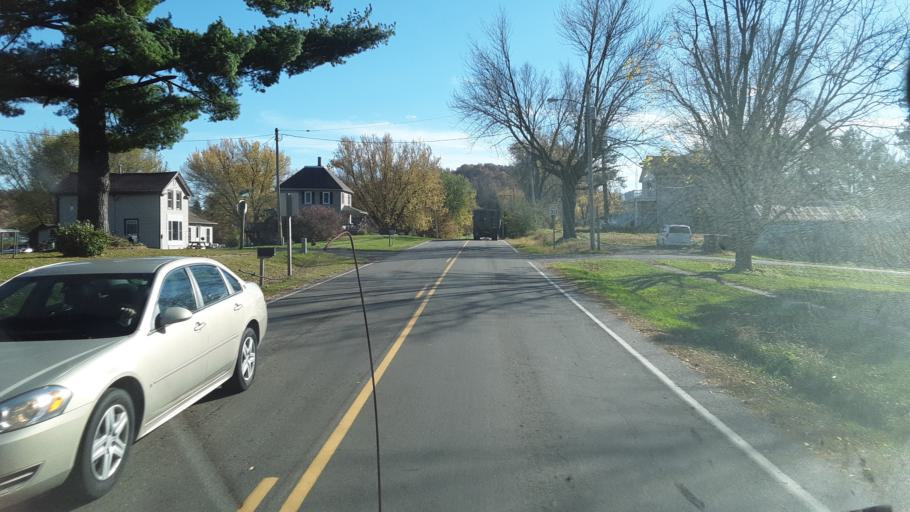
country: US
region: Wisconsin
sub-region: Sauk County
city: Reedsburg
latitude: 43.5448
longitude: -90.1413
